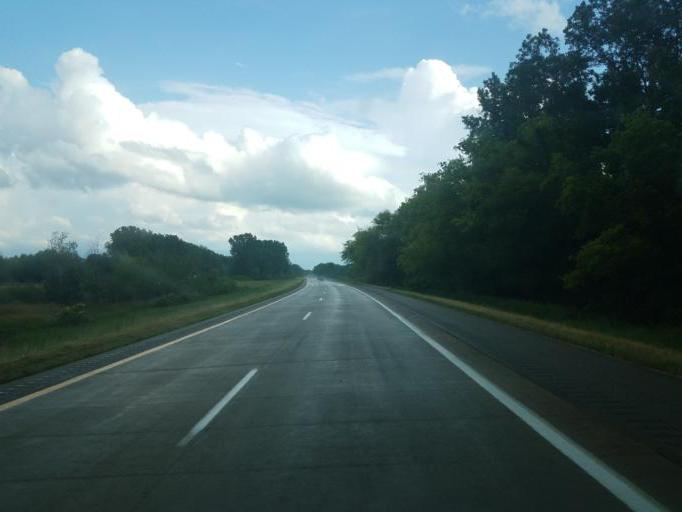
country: US
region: Michigan
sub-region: Calhoun County
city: Marshall
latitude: 42.2357
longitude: -84.9862
